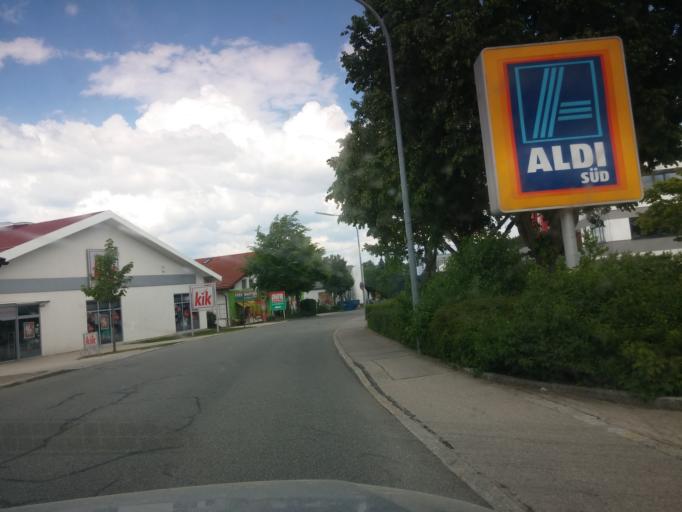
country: DE
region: Bavaria
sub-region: Upper Bavaria
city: Holzkirchen
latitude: 47.8833
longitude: 11.7106
